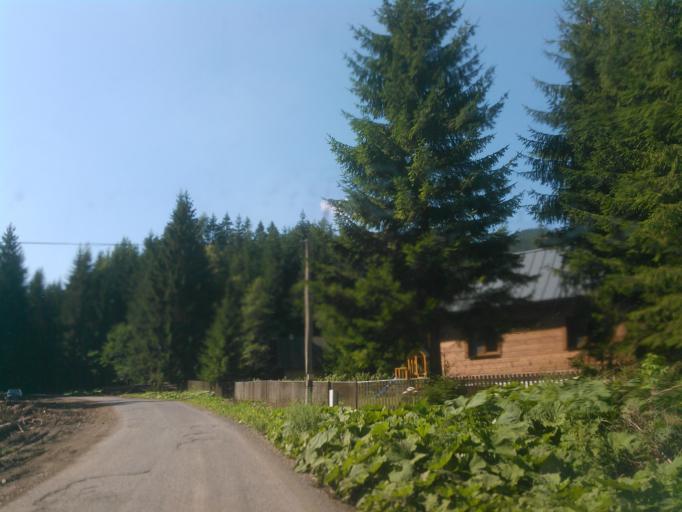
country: SK
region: Zilinsky
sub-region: Okres Liptovsky Mikulas
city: Liptovsky Mikulas
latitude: 48.9999
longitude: 19.5065
